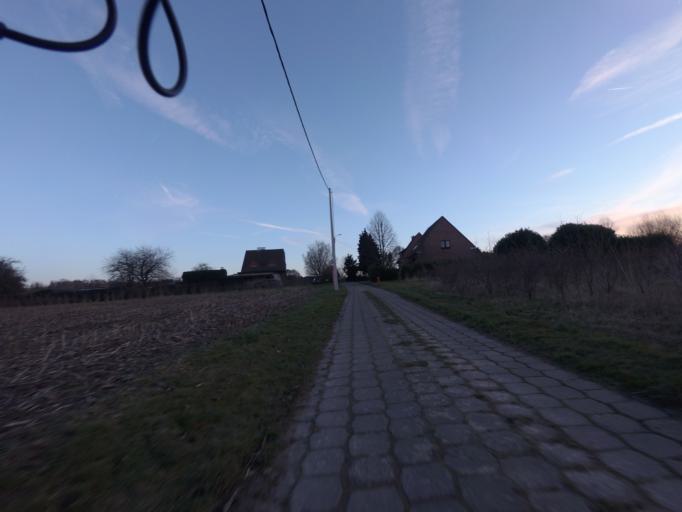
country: BE
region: Flanders
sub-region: Provincie Vlaams-Brabant
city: Grimbergen
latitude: 50.9130
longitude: 4.3836
